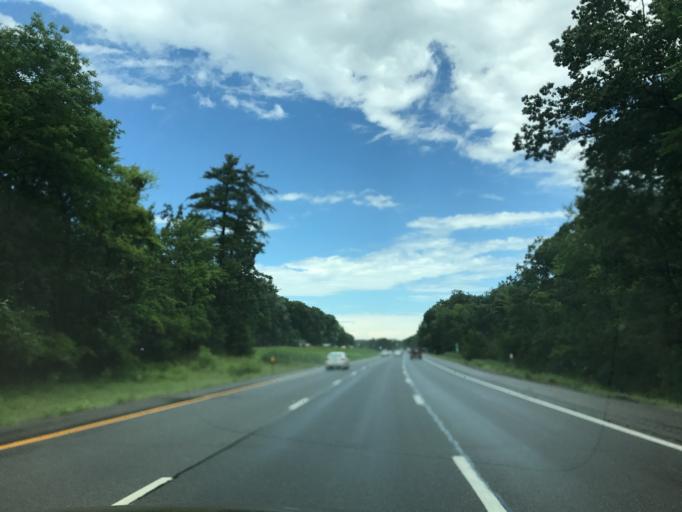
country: US
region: New York
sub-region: Albany County
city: Cohoes
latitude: 42.8276
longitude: -73.7692
